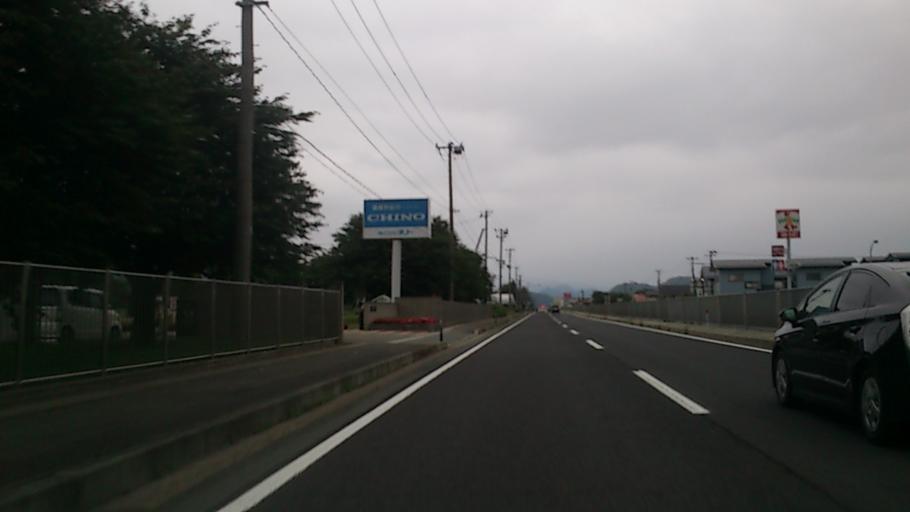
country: JP
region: Yamagata
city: Tendo
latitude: 38.3851
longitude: 140.3819
